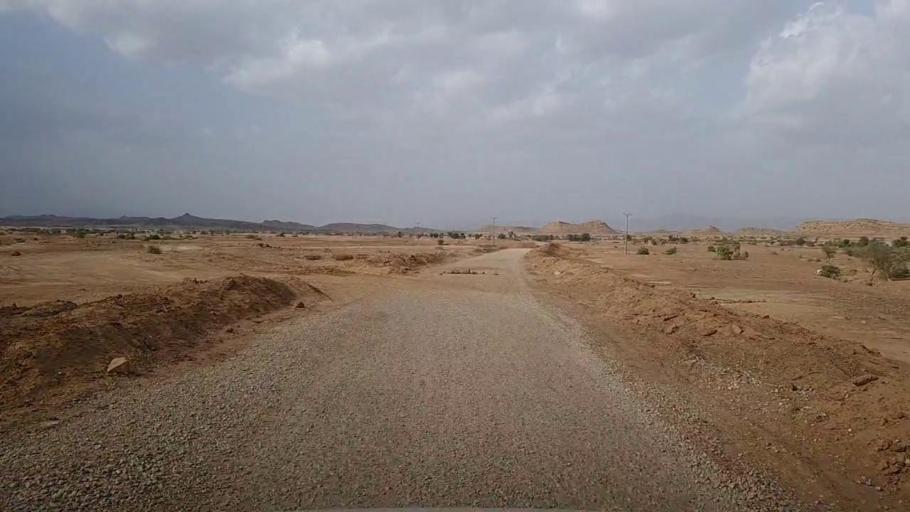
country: PK
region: Sindh
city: Jamshoro
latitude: 25.5060
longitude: 67.6357
